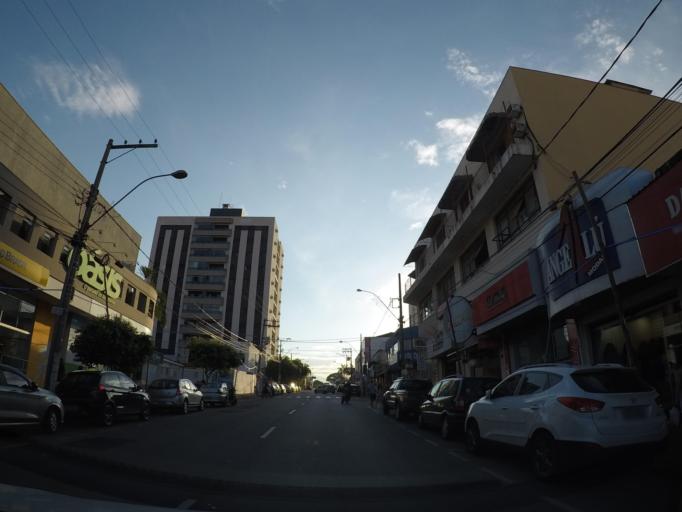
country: BR
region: Sao Paulo
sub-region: Sumare
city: Sumare
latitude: -22.8240
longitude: -47.2676
